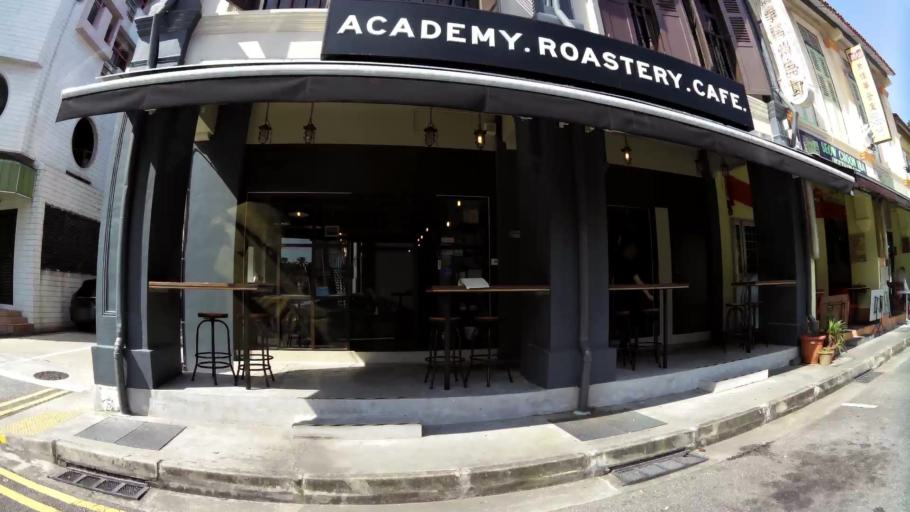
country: SG
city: Singapore
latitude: 1.3015
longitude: 103.8608
